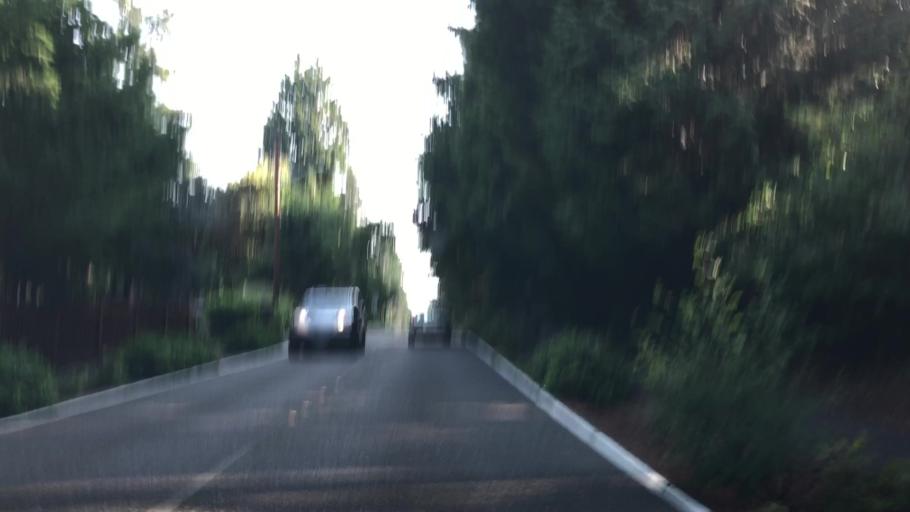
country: US
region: Washington
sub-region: King County
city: Newport
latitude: 47.5856
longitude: -122.1965
